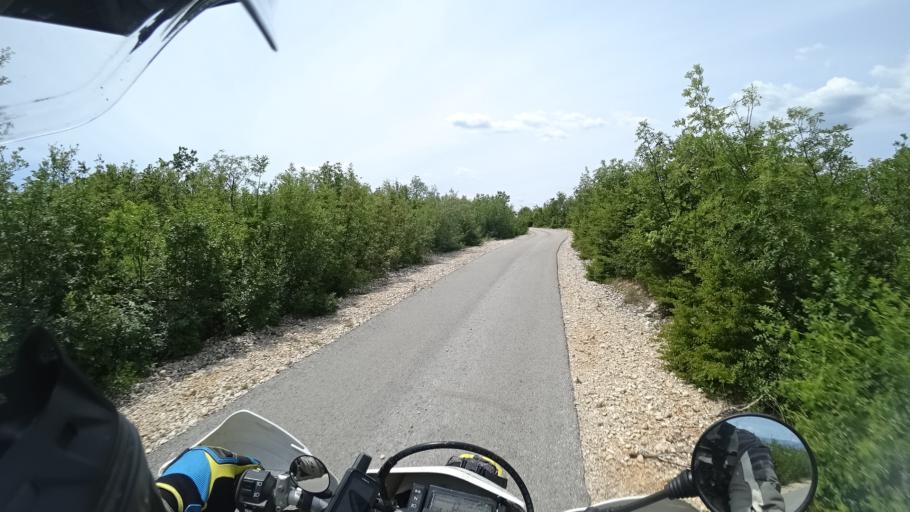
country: HR
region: Sibensko-Kniniska
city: Kistanje
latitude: 44.0601
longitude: 16.0443
